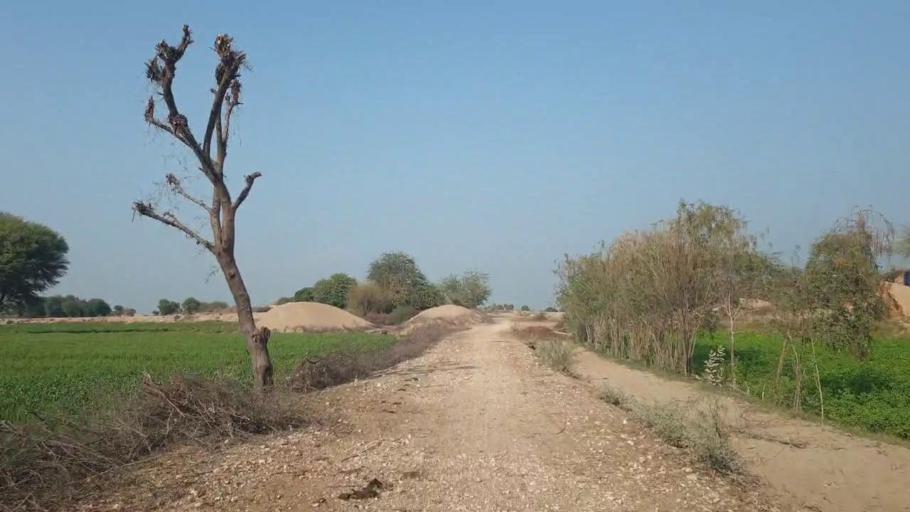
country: PK
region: Sindh
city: Hala
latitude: 25.8351
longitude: 68.4040
